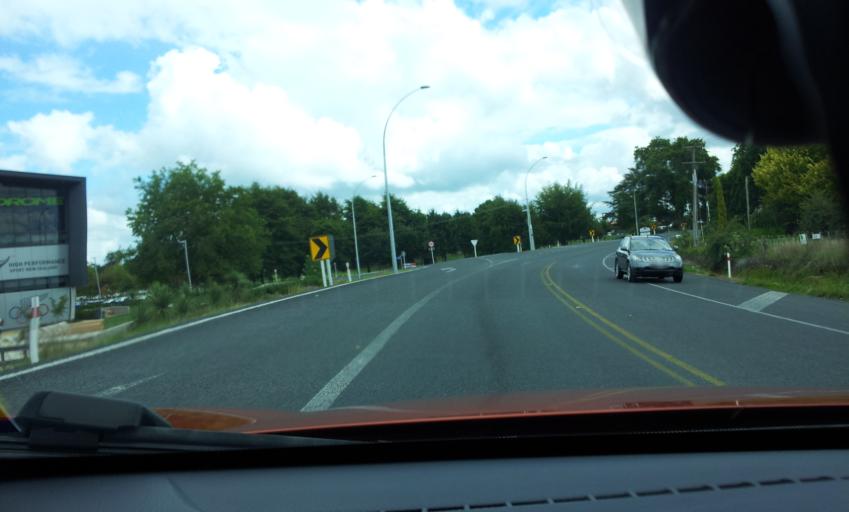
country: NZ
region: Waikato
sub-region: Waipa District
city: Cambridge
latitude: -37.8889
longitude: 175.4357
